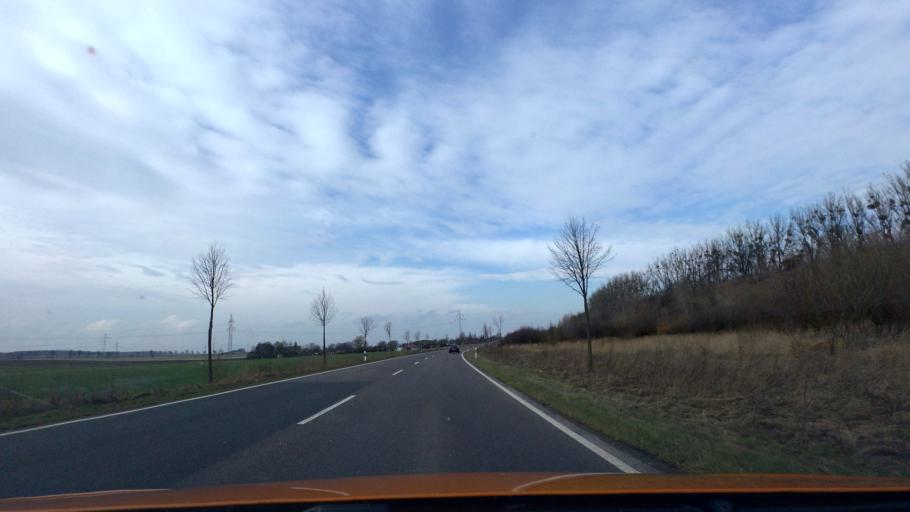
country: DE
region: Lower Saxony
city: Helmstedt
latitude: 52.2174
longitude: 10.9967
